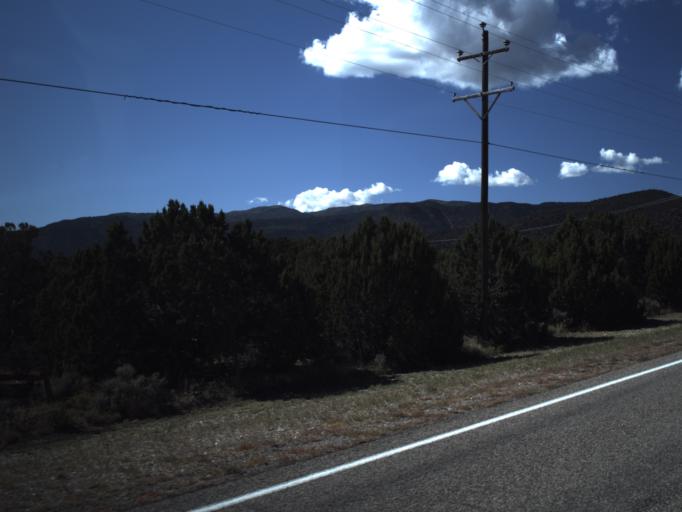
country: US
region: Utah
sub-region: Iron County
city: Cedar City
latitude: 37.6434
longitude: -113.2492
